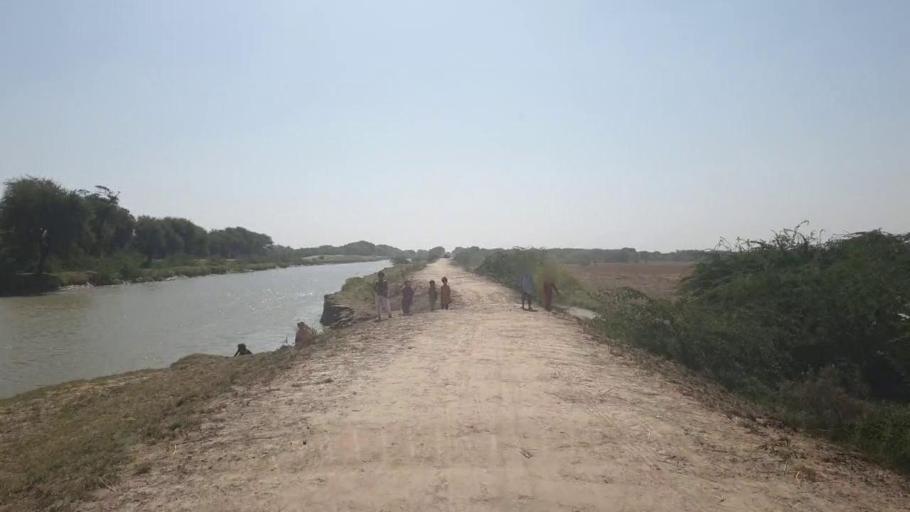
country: PK
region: Sindh
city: Talhar
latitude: 24.8188
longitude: 68.7935
